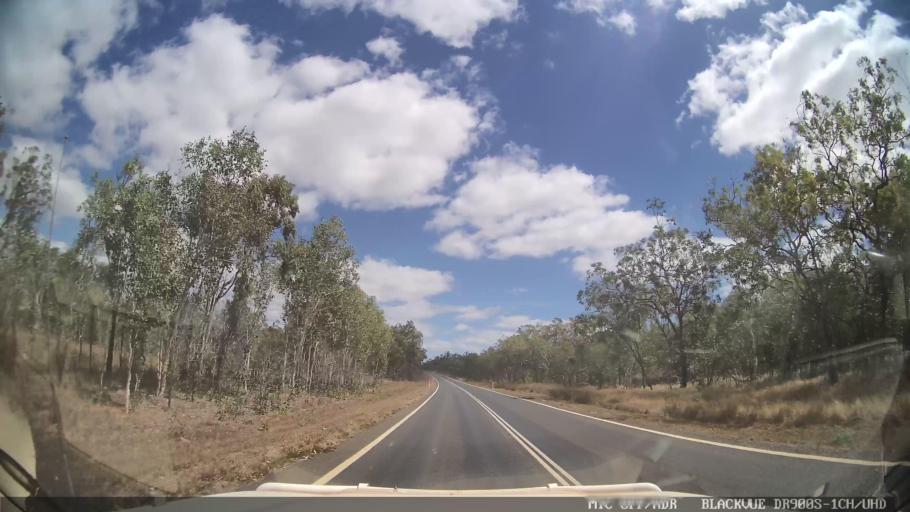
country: AU
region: Queensland
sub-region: Tablelands
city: Ravenshoe
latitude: -17.9067
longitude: 144.8843
